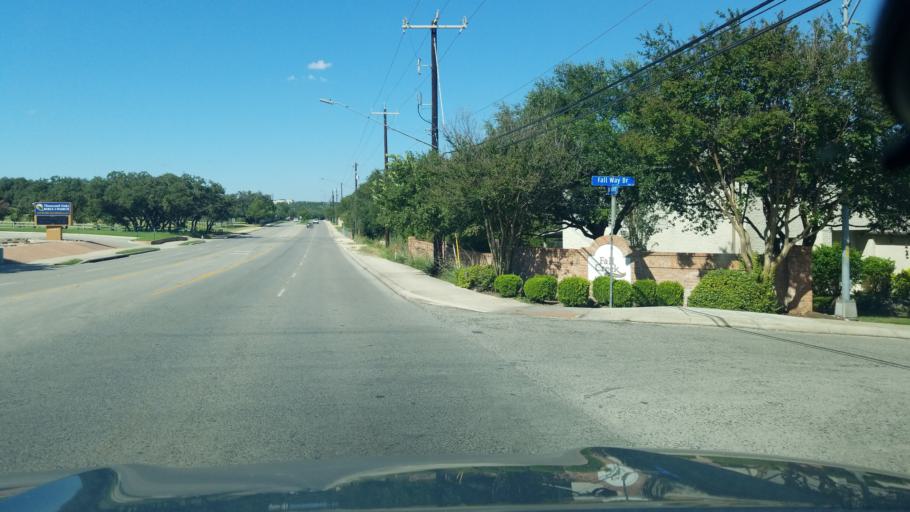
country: US
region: Texas
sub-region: Bexar County
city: Hollywood Park
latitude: 29.5832
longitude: -98.4385
